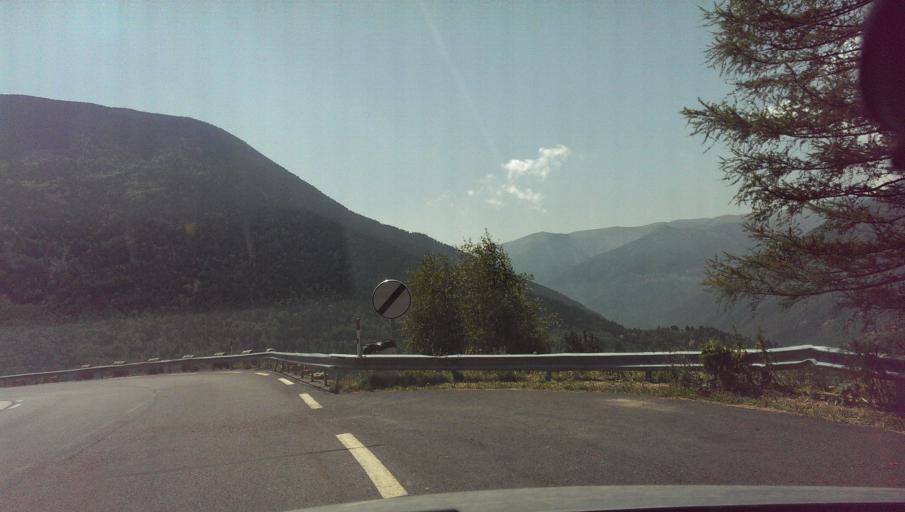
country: AD
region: Encamp
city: Pas de la Casa
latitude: 42.5514
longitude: 1.8330
